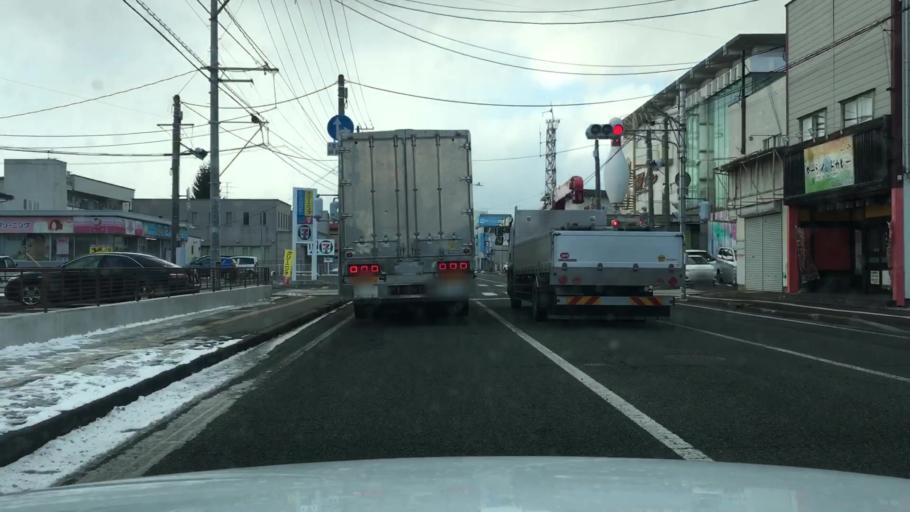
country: JP
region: Iwate
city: Morioka-shi
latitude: 39.6923
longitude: 141.1716
